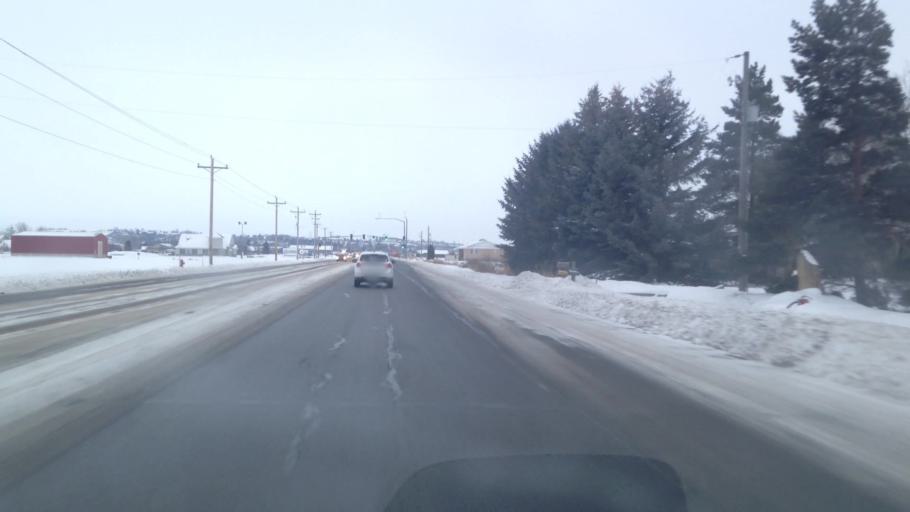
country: US
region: Idaho
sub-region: Madison County
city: Rexburg
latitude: 43.8542
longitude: -111.7780
